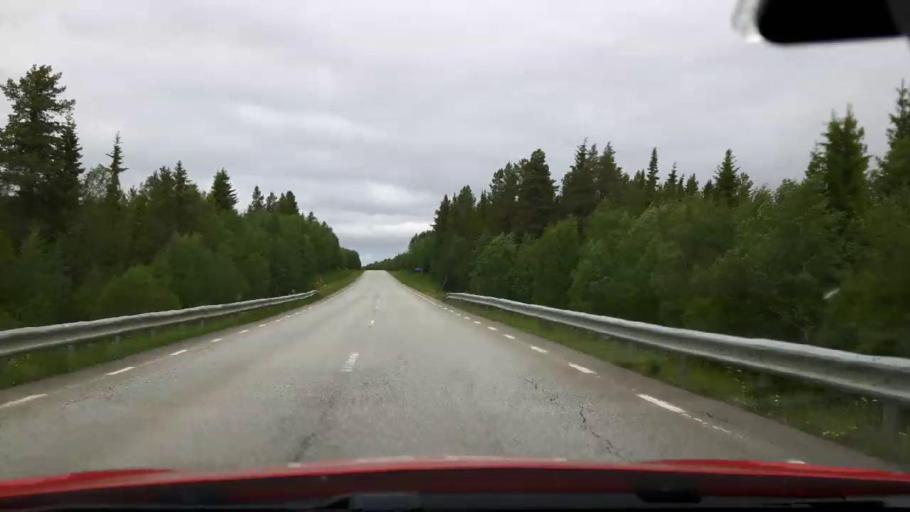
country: SE
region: Jaemtland
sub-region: OEstersunds Kommun
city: Lit
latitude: 63.6136
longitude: 14.6750
